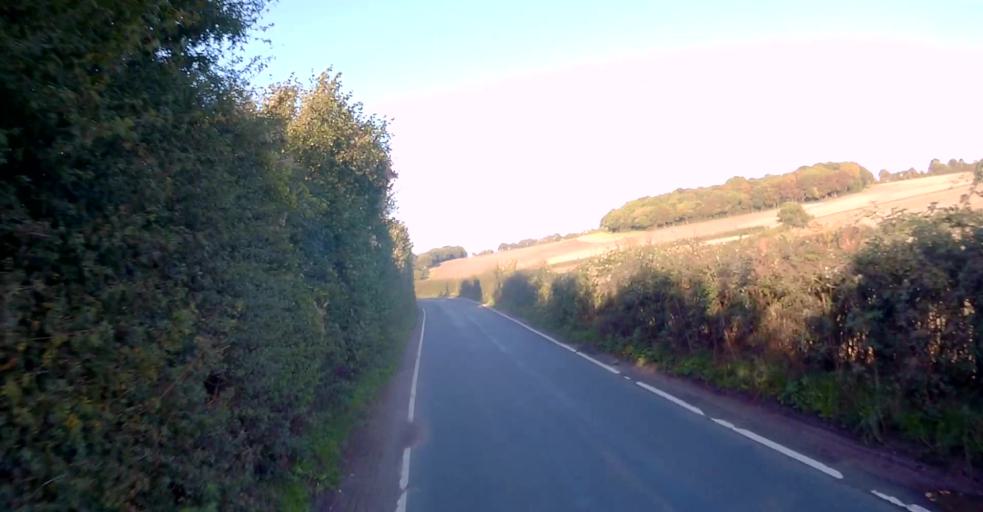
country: GB
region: England
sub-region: Hampshire
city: Long Sutton
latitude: 51.2351
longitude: -0.9256
